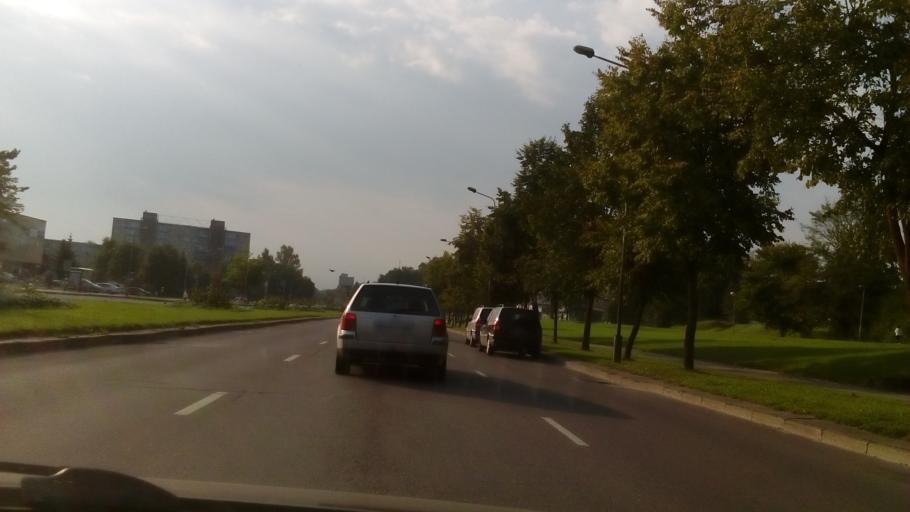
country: LT
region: Alytaus apskritis
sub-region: Alytus
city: Alytus
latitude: 54.4027
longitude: 24.0217
